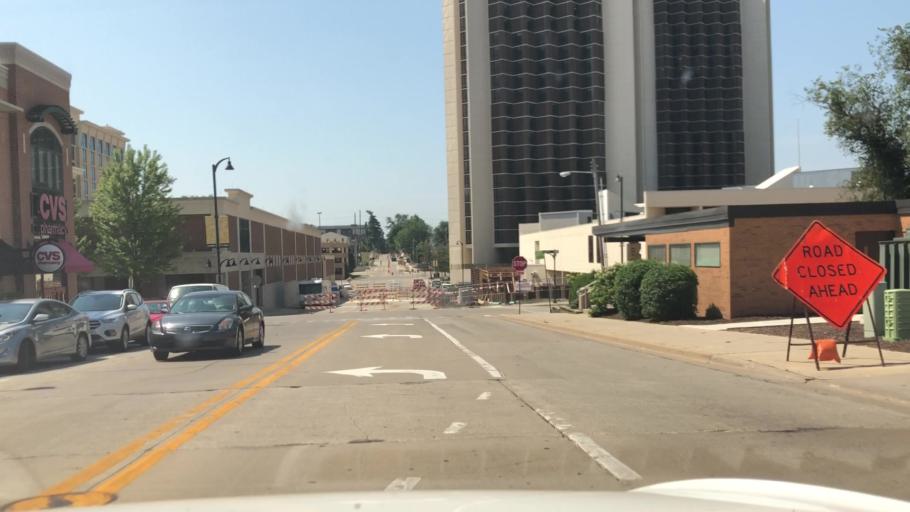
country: US
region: Illinois
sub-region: McLean County
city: Normal
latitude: 40.5099
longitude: -88.9872
